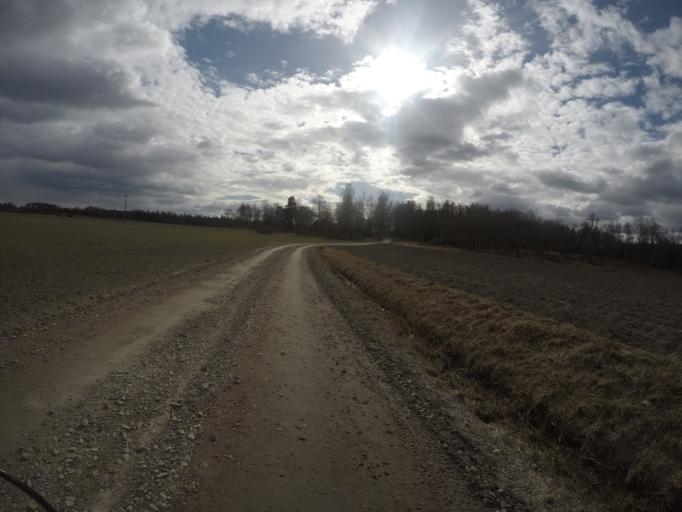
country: SE
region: Soedermanland
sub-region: Eskilstuna Kommun
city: Kvicksund
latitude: 59.4395
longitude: 16.3017
